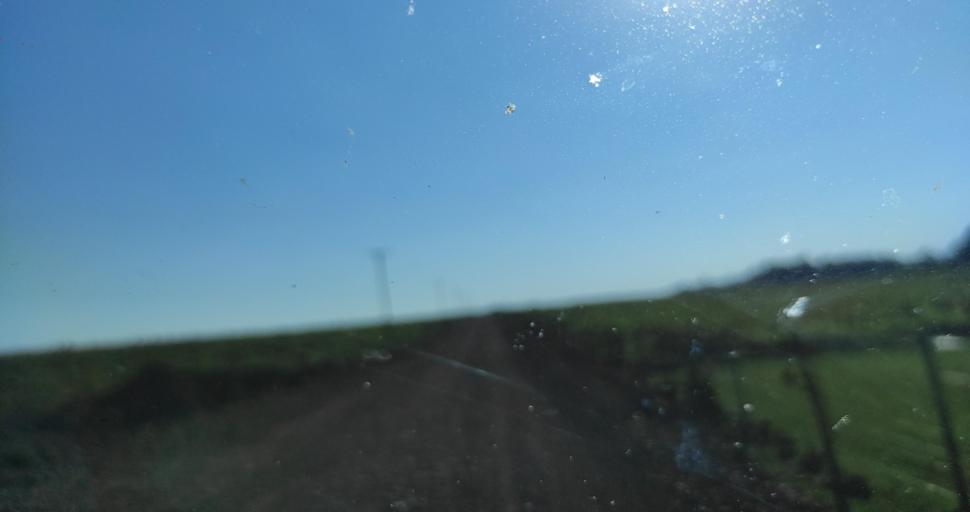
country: PY
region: Itapua
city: Carmen del Parana
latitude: -27.4119
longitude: -56.1471
